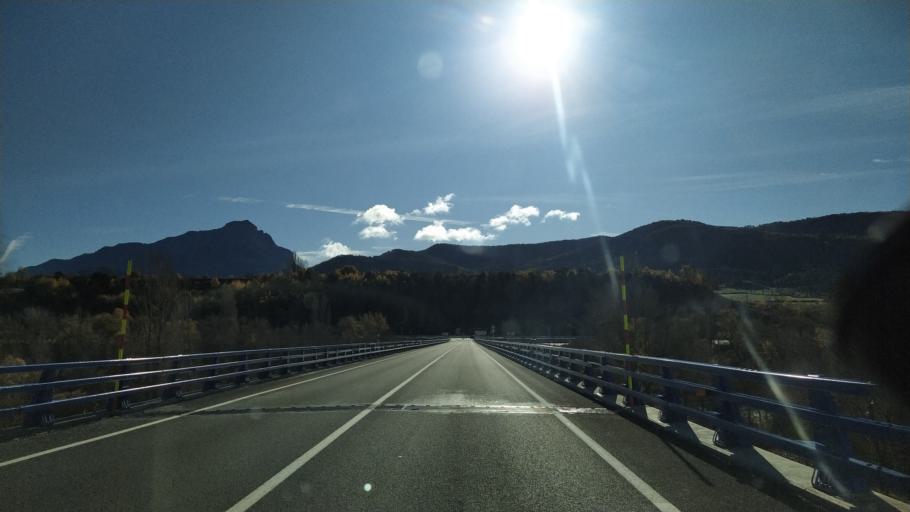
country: ES
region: Aragon
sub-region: Provincia de Huesca
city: Jaca
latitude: 42.5621
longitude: -0.5940
